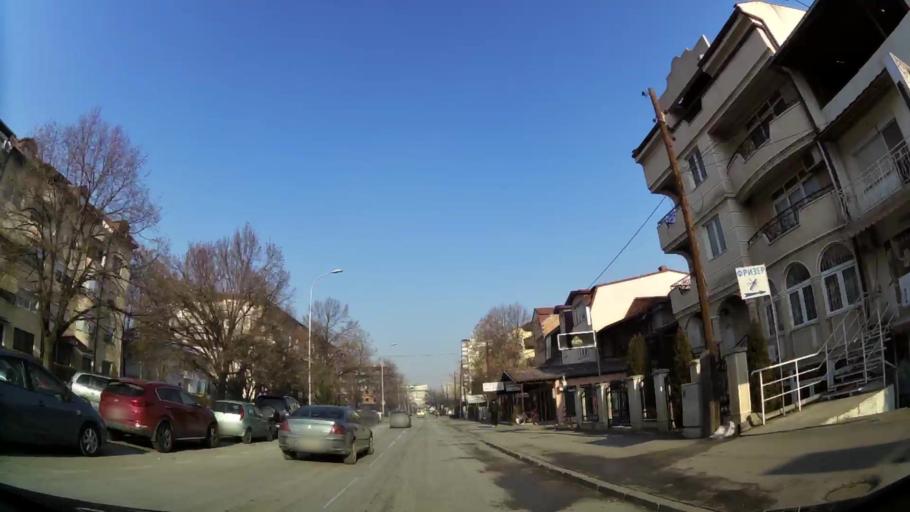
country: MK
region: Karpos
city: Skopje
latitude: 41.9778
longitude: 21.4424
